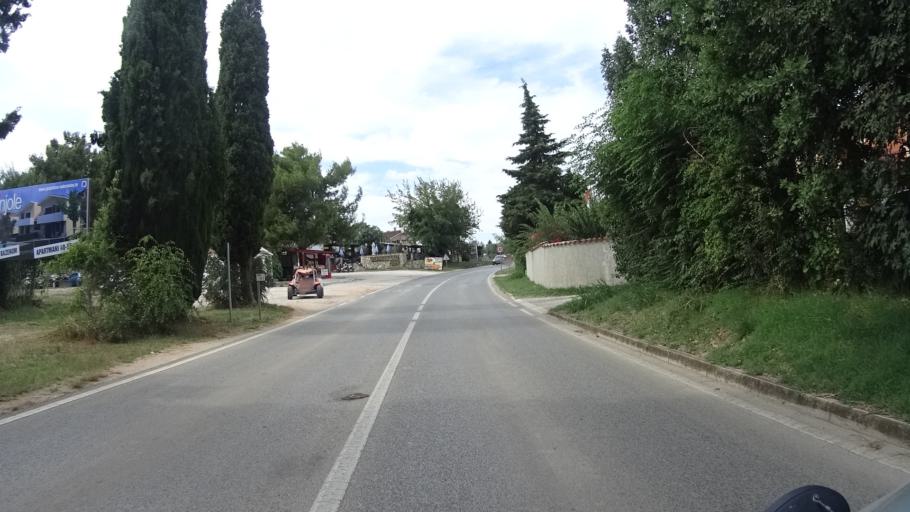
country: HR
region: Istarska
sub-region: Grad Pula
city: Pula
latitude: 44.8241
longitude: 13.8789
